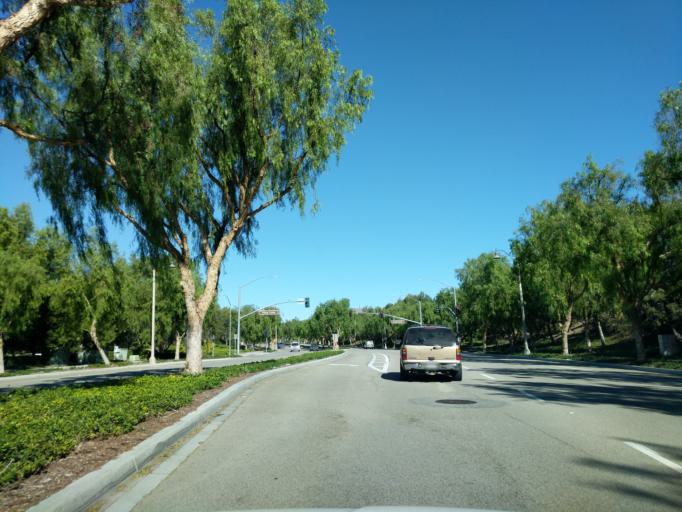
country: US
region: California
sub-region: Orange County
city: North Tustin
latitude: 33.7335
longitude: -117.7590
